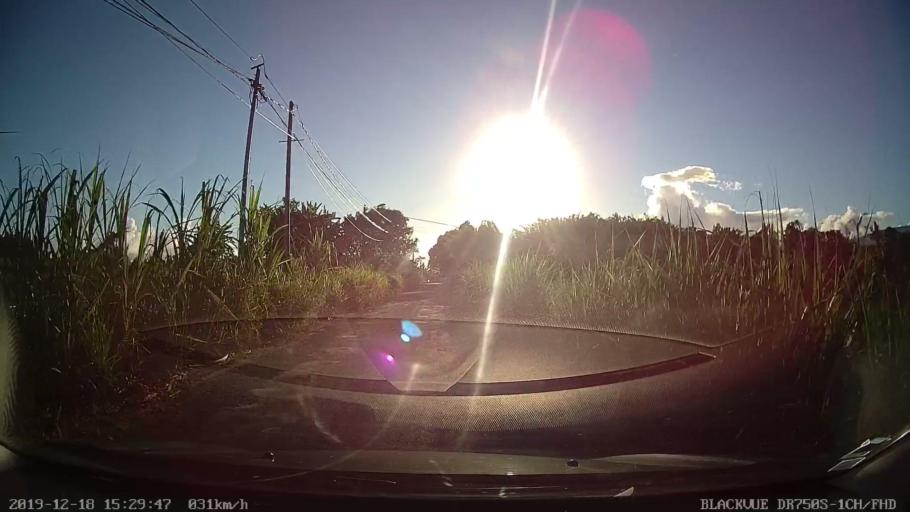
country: RE
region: Reunion
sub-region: Reunion
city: Bras-Panon
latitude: -20.9988
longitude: 55.6632
